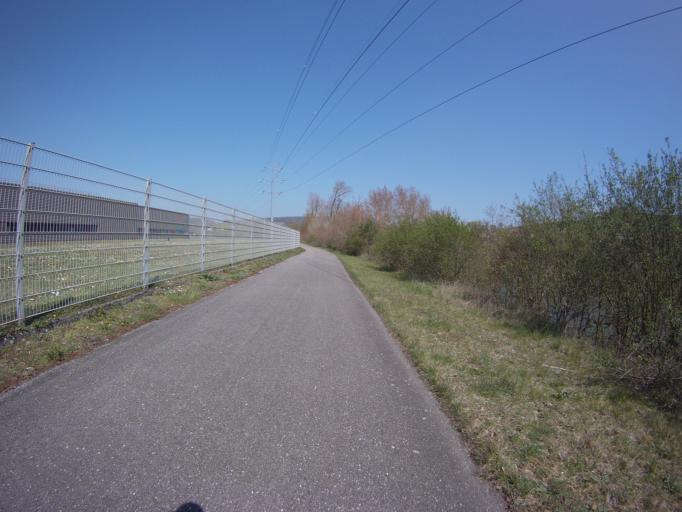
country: FR
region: Lorraine
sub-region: Departement de Meurthe-et-Moselle
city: Custines
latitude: 48.7824
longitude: 6.1420
